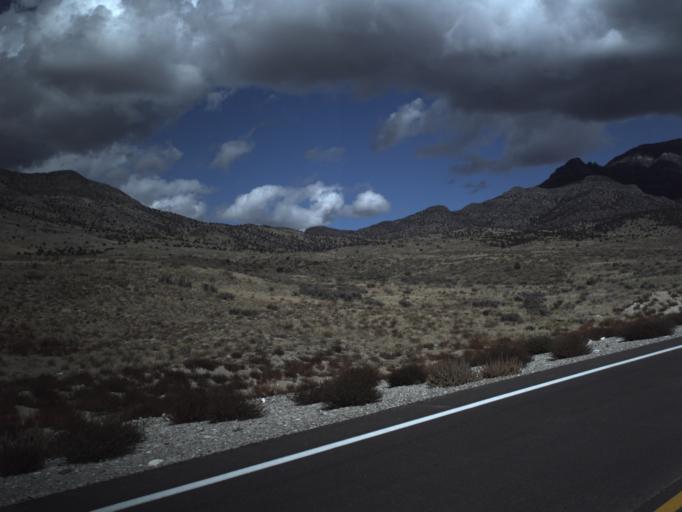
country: US
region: Utah
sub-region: Beaver County
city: Milford
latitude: 38.5109
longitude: -113.5852
